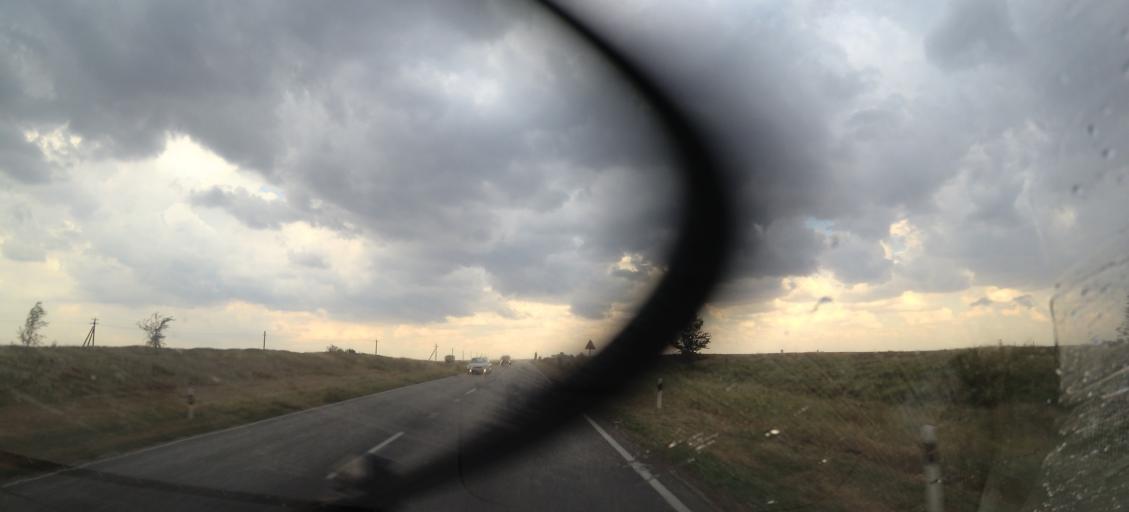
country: RU
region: Rostov
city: Orlovskiy
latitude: 46.8739
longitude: 41.9901
